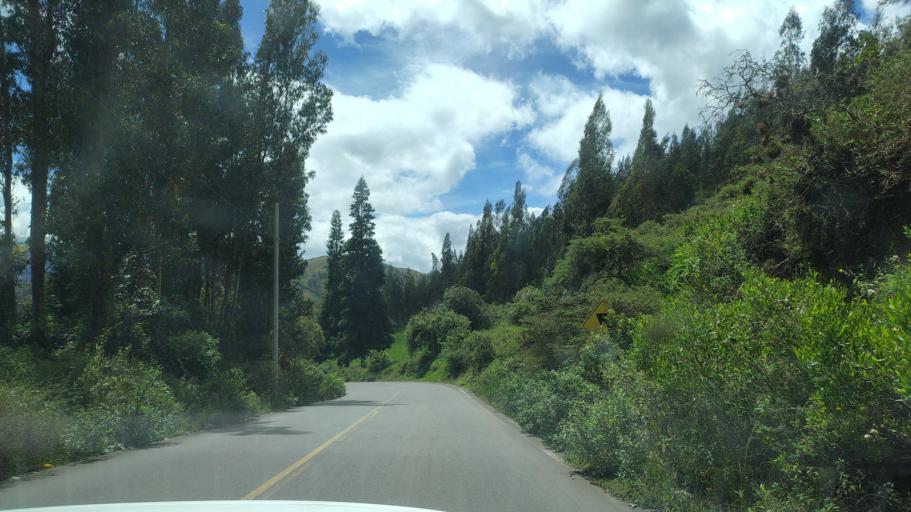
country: EC
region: Chimborazo
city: Riobamba
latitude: -1.6610
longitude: -78.5844
